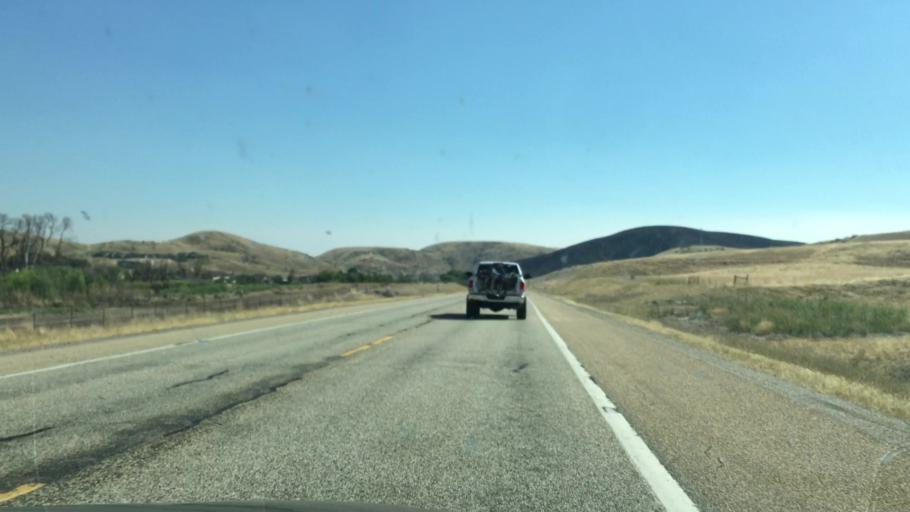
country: US
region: Idaho
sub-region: Ada County
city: Eagle
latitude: 43.7820
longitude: -116.2639
